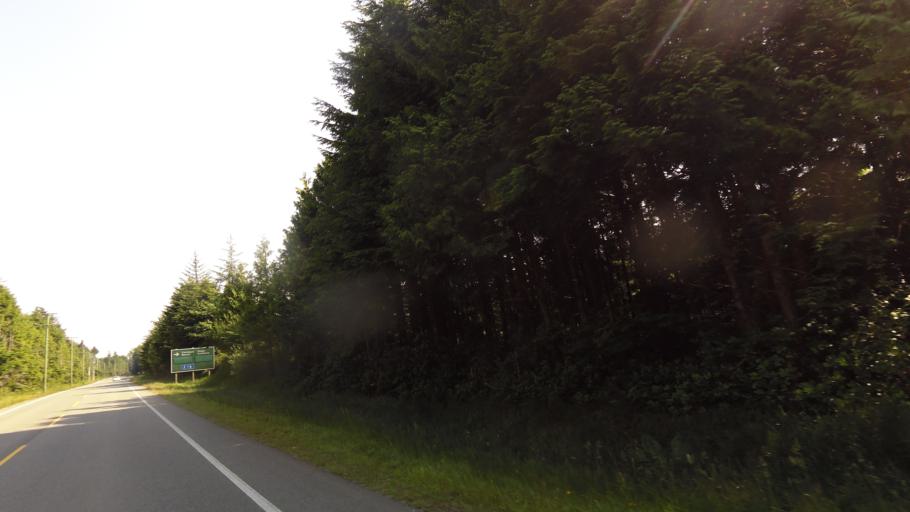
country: CA
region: British Columbia
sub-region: Regional District of Alberni-Clayoquot
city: Ucluelet
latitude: 49.0482
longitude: -125.7045
